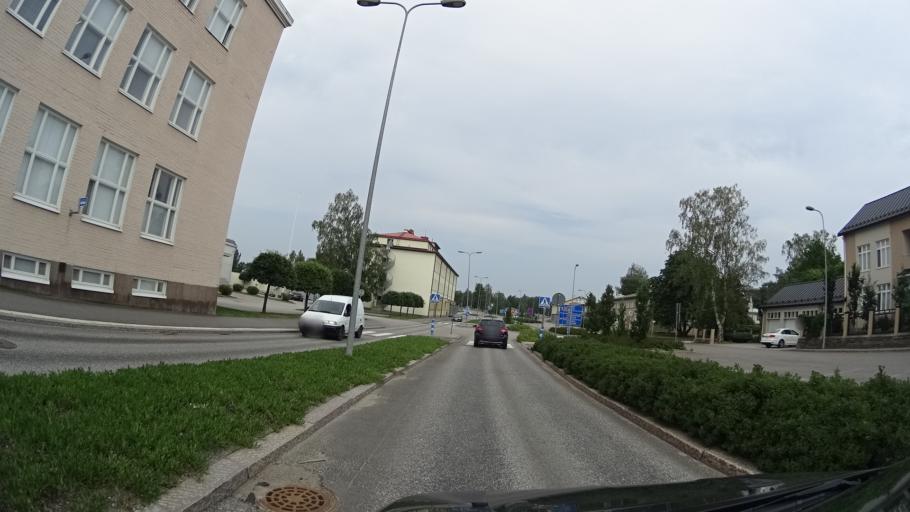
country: FI
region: Uusimaa
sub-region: Raaseporin
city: Ekenaes
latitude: 59.9805
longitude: 23.4398
